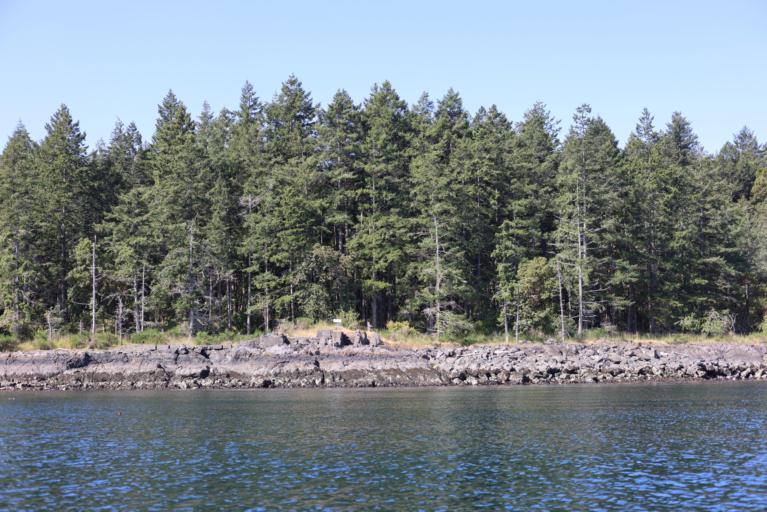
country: CA
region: British Columbia
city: Colwood
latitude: 48.3920
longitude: -123.4835
